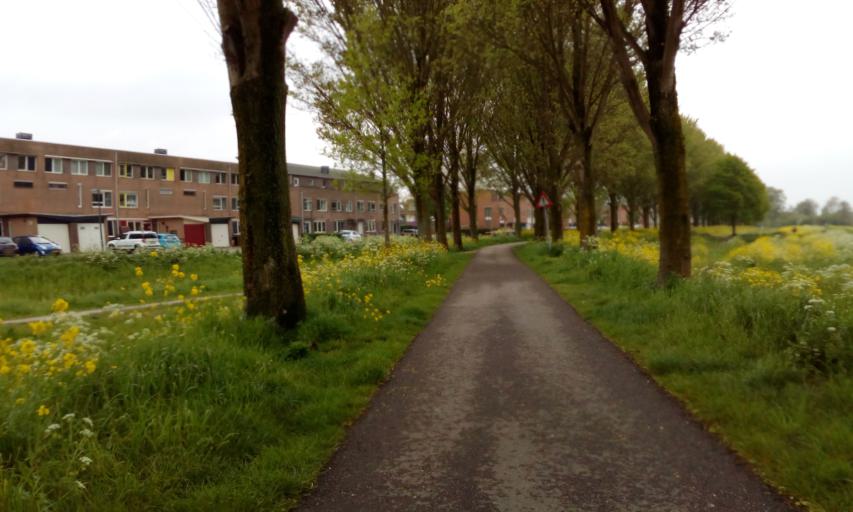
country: NL
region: South Holland
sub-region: Gemeente Schiedam
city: Schiedam
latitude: 51.9488
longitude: 4.3788
